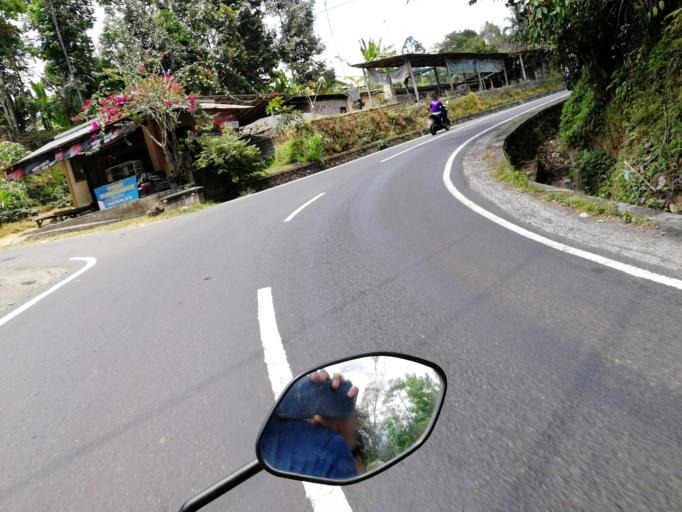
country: ID
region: Bali
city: Banjar Geriana Kangin
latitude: -8.4276
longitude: 115.4376
